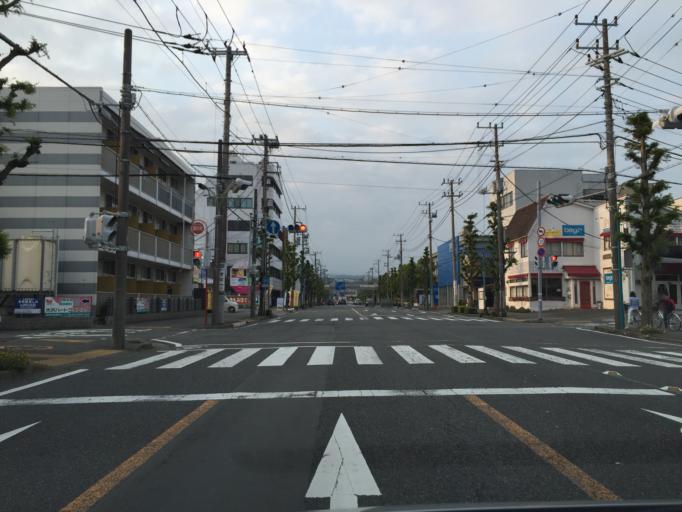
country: JP
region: Shizuoka
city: Numazu
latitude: 35.1177
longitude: 138.8601
